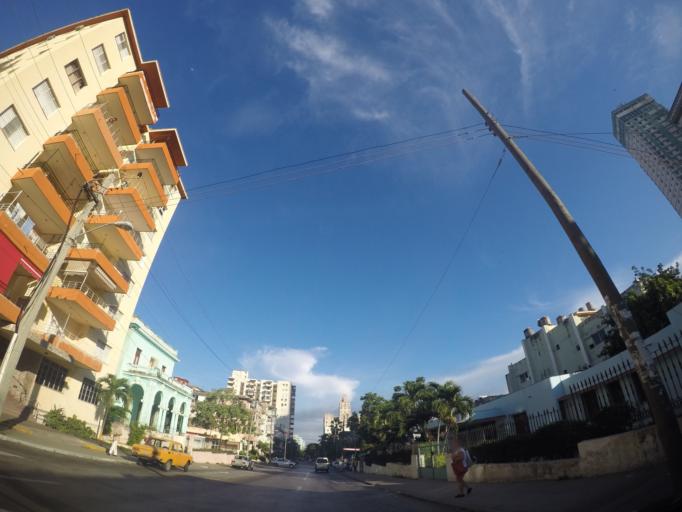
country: CU
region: La Habana
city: Havana
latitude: 23.1420
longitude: -82.3854
